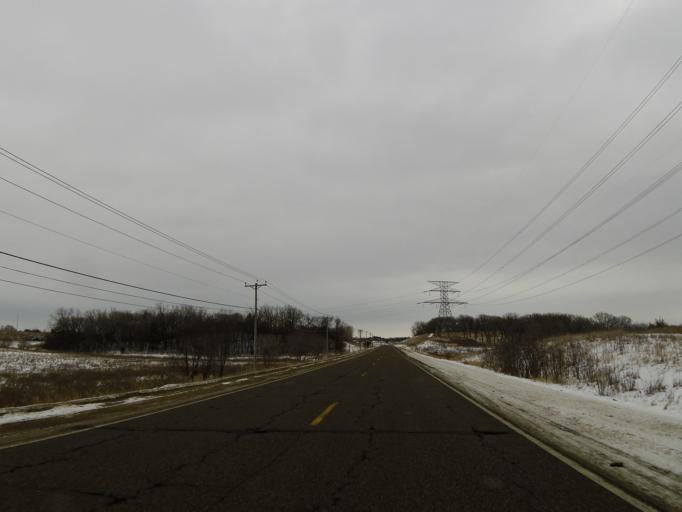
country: US
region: Minnesota
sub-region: Washington County
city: Lakeland
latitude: 44.9469
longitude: -92.8257
